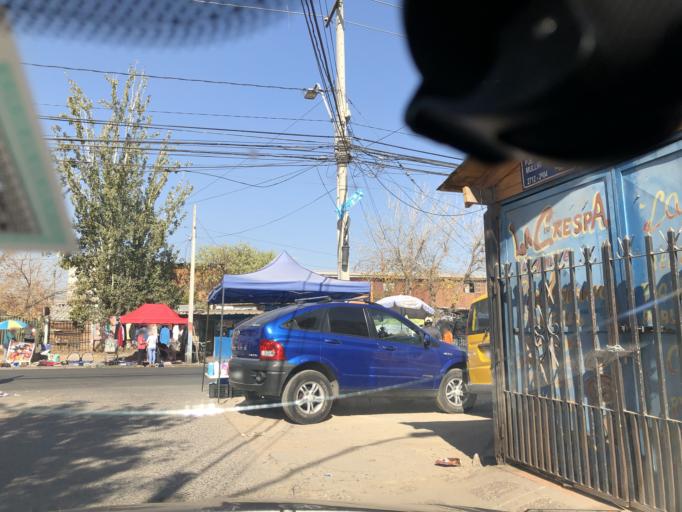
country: CL
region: Santiago Metropolitan
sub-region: Provincia de Santiago
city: La Pintana
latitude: -33.5879
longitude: -70.6006
